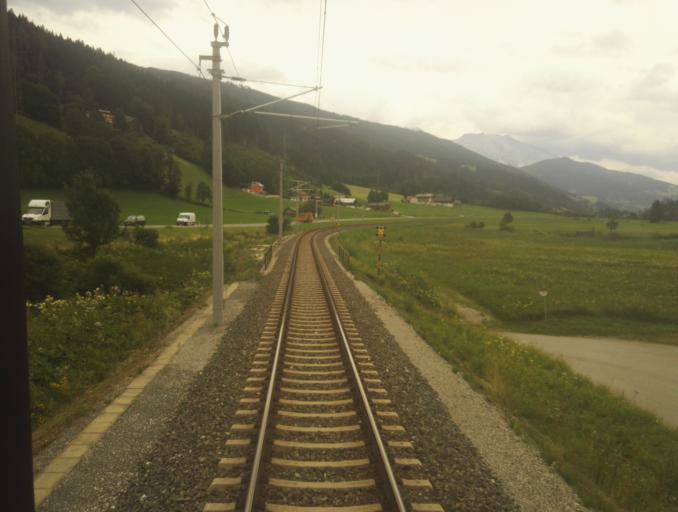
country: AT
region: Salzburg
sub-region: Politischer Bezirk Sankt Johann im Pongau
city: Forstau
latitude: 47.3884
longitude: 13.4958
